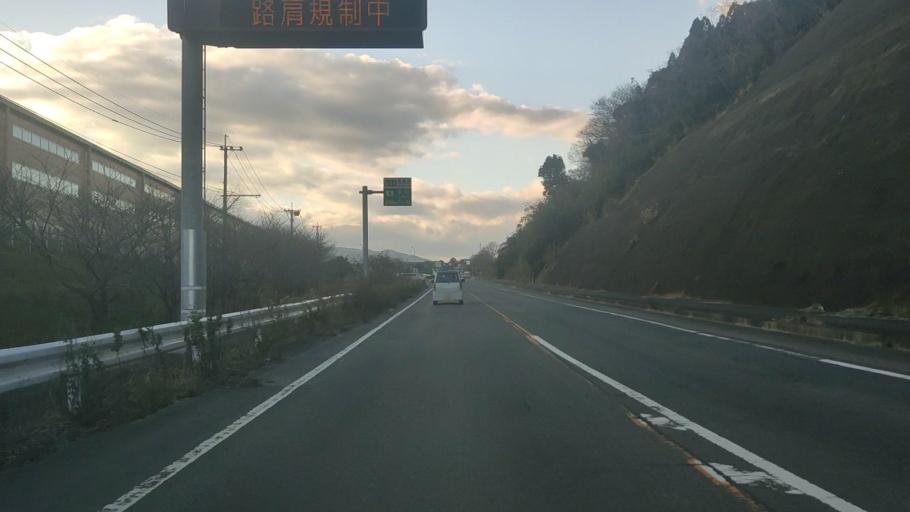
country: JP
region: Saga Prefecture
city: Takeocho-takeo
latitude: 33.2897
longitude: 130.1286
